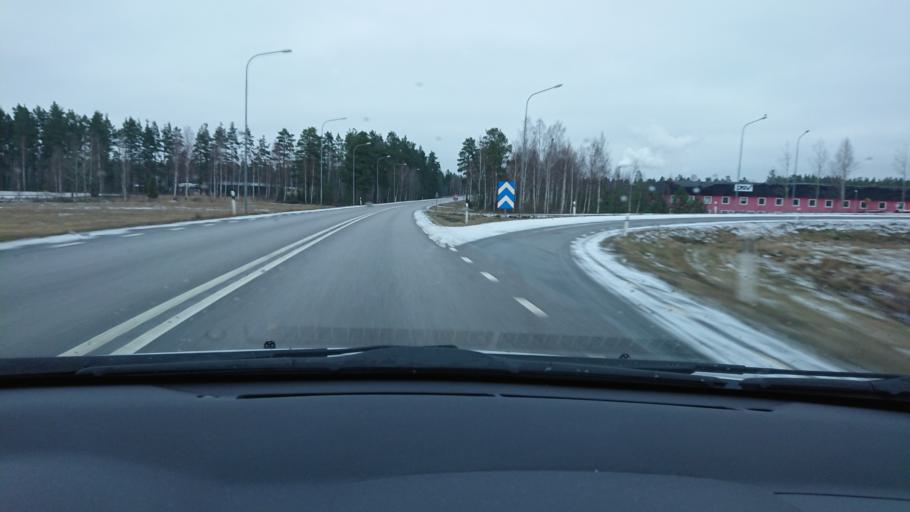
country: SE
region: Kalmar
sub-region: Hultsfreds Kommun
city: Hultsfred
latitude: 57.5010
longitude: 15.8222
